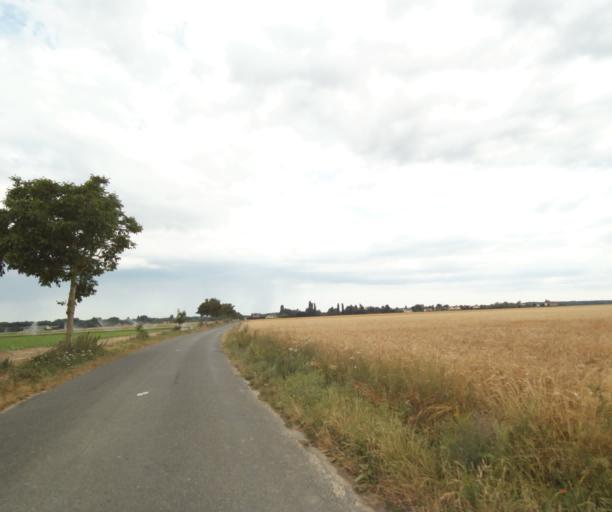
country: FR
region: Ile-de-France
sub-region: Departement de Seine-et-Marne
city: Arbonne-la-Foret
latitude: 48.4299
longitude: 2.5598
